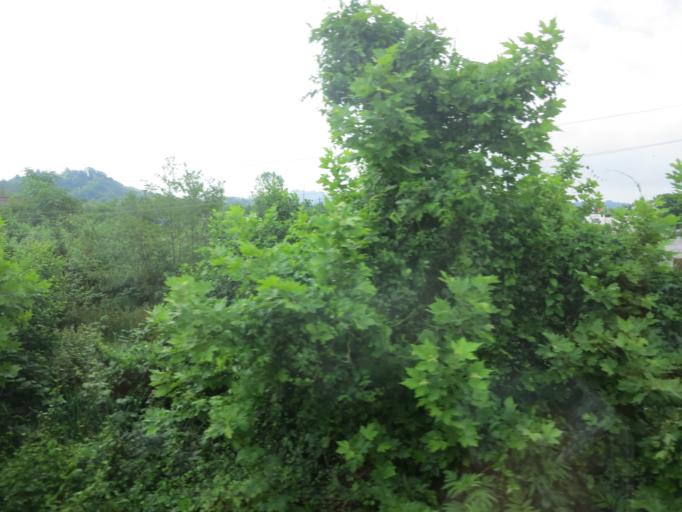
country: GE
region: Guria
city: Urek'i
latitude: 42.0482
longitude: 41.8191
